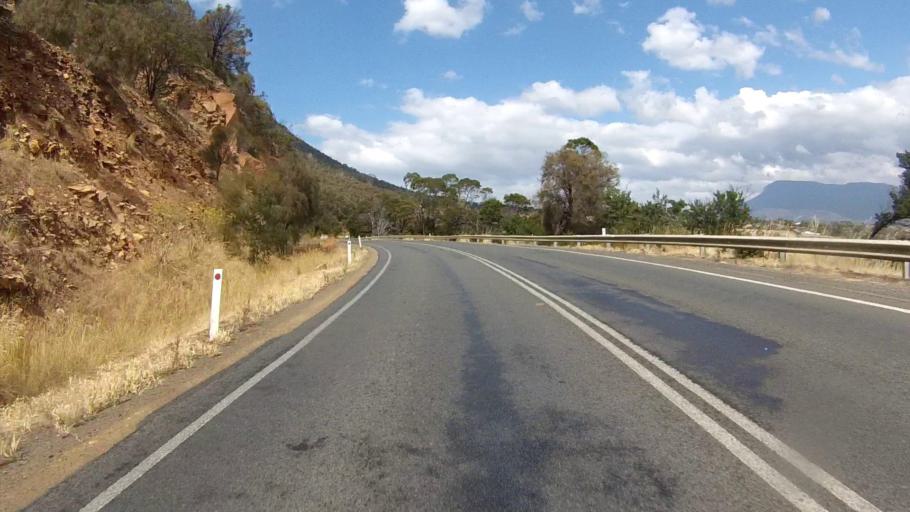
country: AU
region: Tasmania
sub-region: Brighton
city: Old Beach
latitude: -42.7874
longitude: 147.2914
